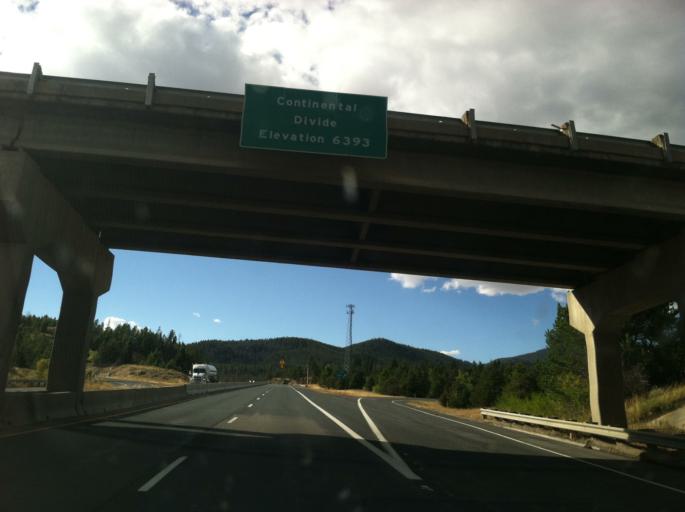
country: US
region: Montana
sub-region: Silver Bow County
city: Butte
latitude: 45.9187
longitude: -112.4101
